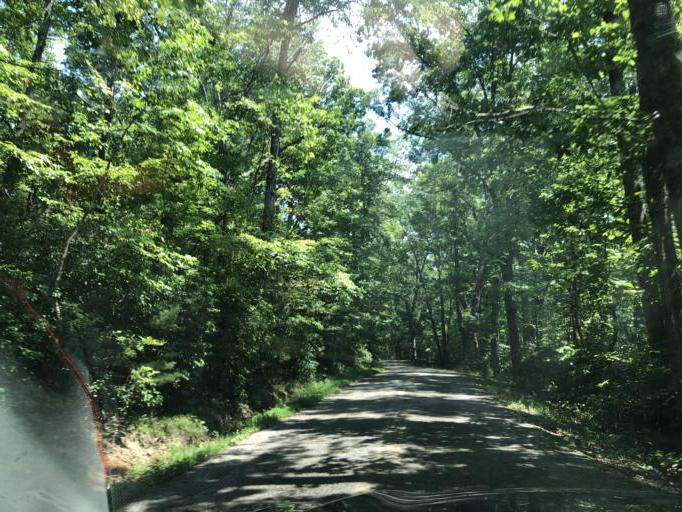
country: US
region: Tennessee
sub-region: Franklin County
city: Sewanee
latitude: 35.2025
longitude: -85.9311
